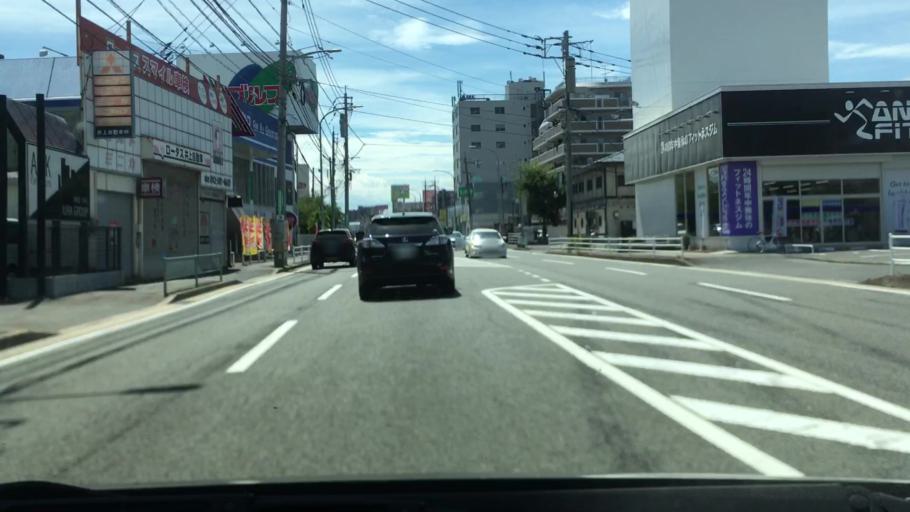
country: JP
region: Fukuoka
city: Onojo
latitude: 33.5540
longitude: 130.4549
